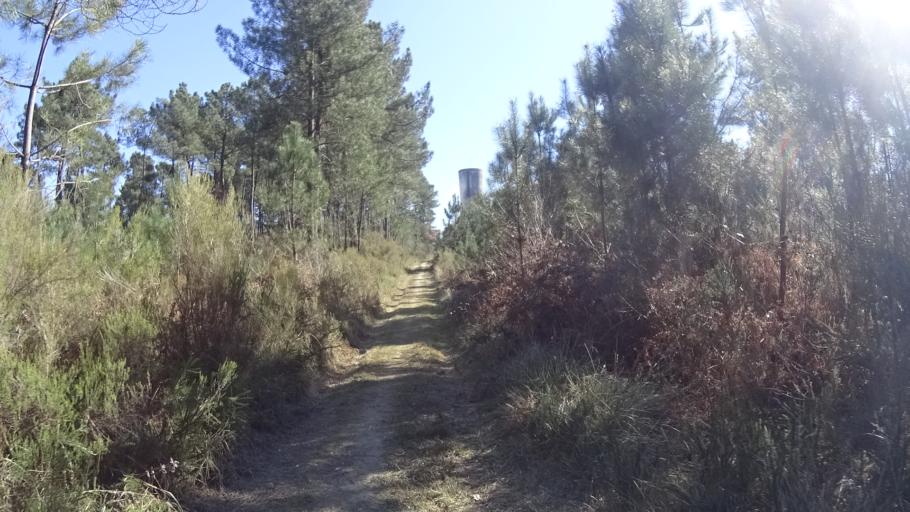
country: FR
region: Aquitaine
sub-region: Departement de la Dordogne
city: Saint-Aulaye
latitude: 45.1313
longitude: 0.2129
